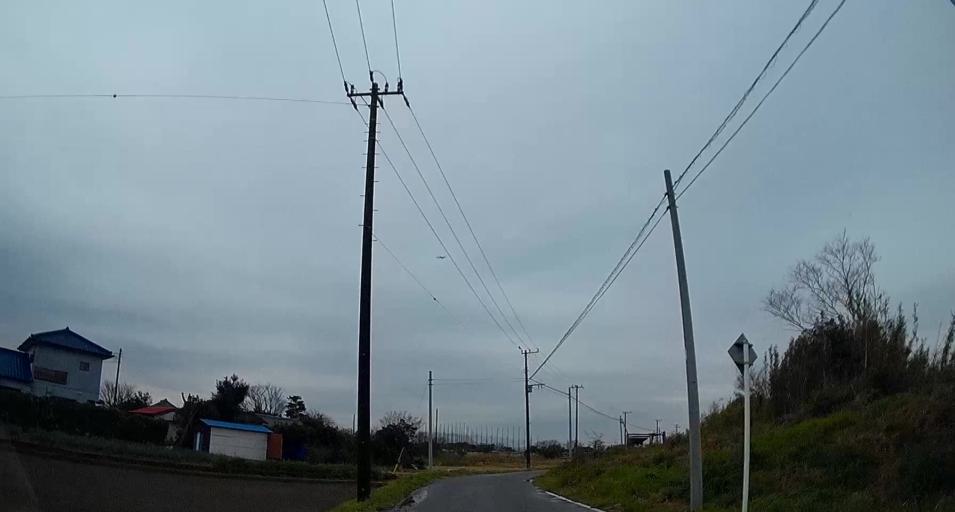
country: JP
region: Chiba
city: Kisarazu
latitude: 35.4123
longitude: 139.9080
